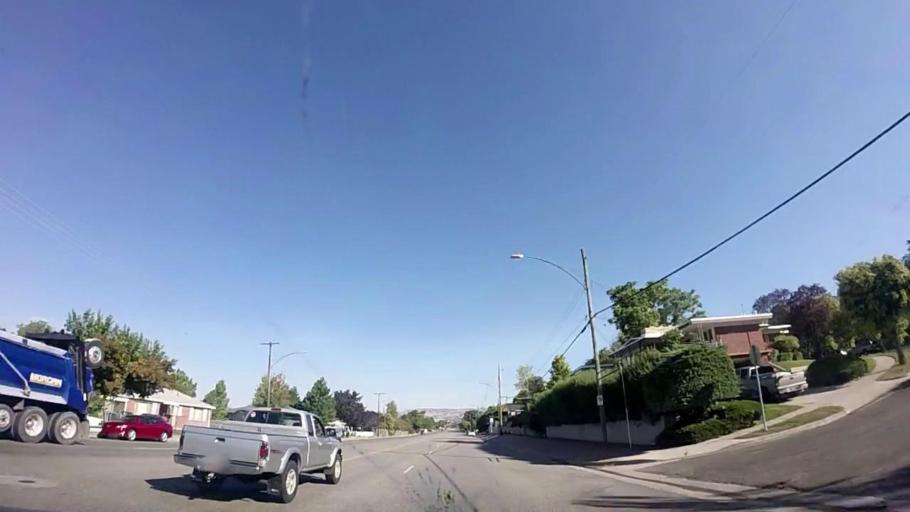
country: US
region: Utah
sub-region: Salt Lake County
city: Canyon Rim
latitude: 40.7278
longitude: -111.8161
